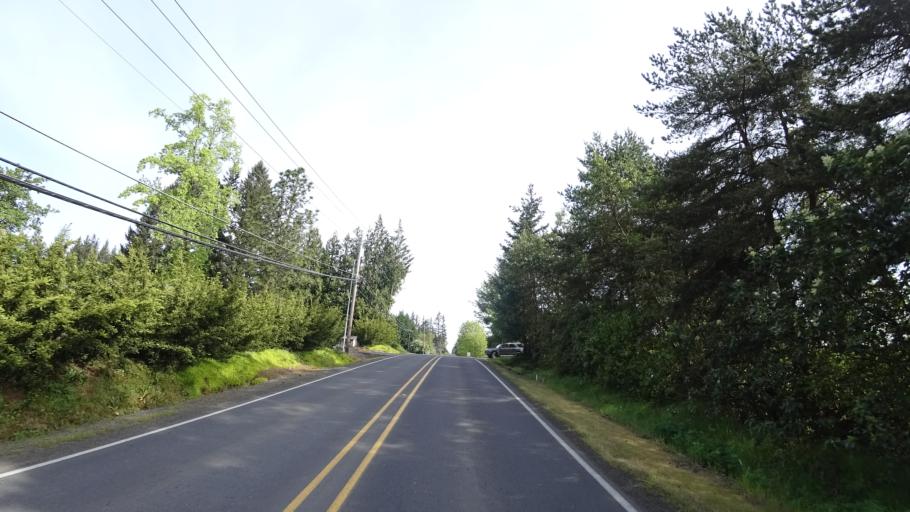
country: US
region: Oregon
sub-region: Washington County
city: Aloha
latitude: 45.4407
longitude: -122.8568
